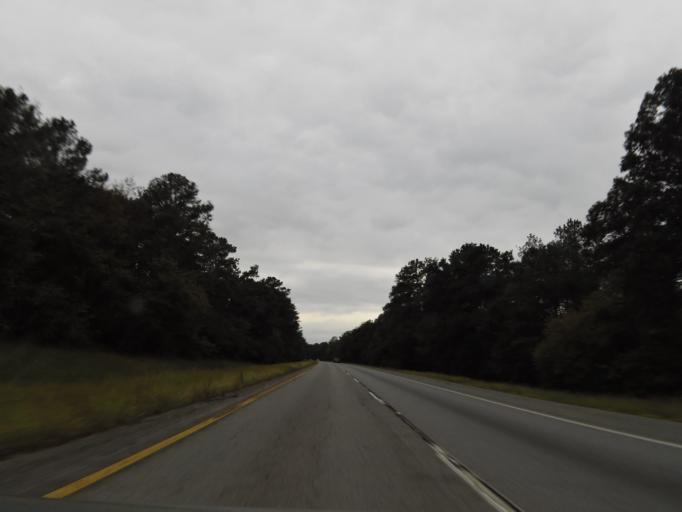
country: US
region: Alabama
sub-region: Saint Clair County
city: Ashville
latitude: 33.8853
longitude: -86.2554
